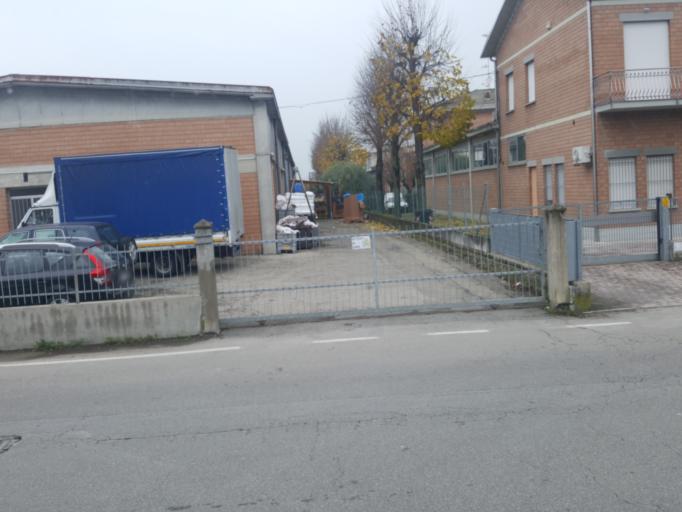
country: IT
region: Emilia-Romagna
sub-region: Provincia di Reggio Emilia
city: Codemondo-Quaresimo
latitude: 44.7181
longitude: 10.5518
